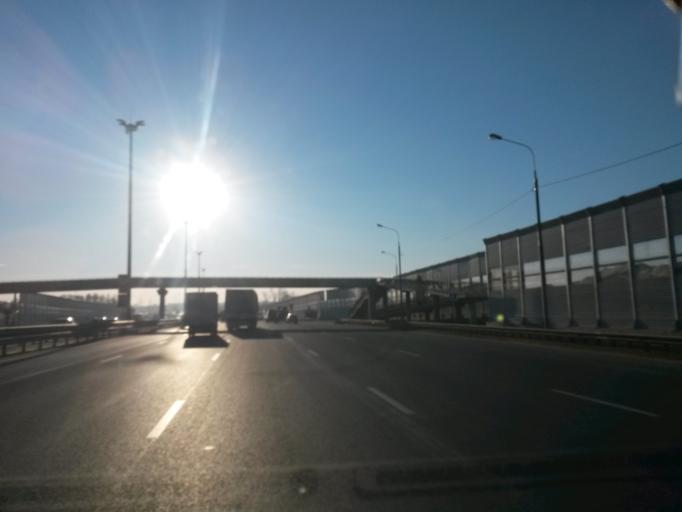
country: RU
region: Moskovskaya
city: Lesnyye Polyany
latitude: 55.9709
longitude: 37.8470
